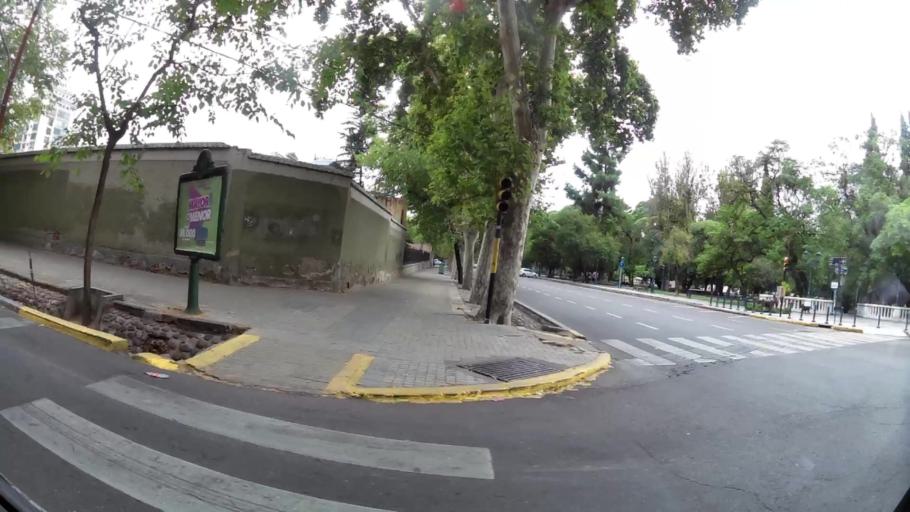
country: AR
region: Mendoza
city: Mendoza
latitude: -32.8906
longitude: -68.8461
